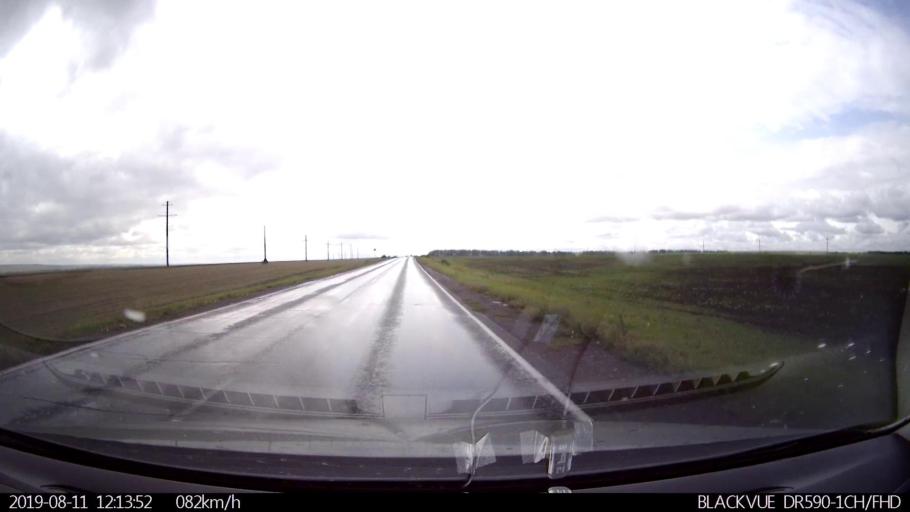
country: RU
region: Ulyanovsk
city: Ignatovka
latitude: 53.9577
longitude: 47.9875
